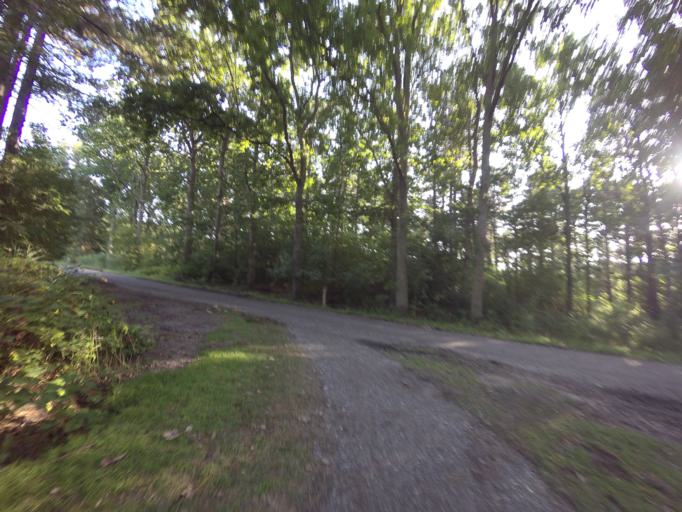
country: NL
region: Friesland
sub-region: Gemeente Terschelling
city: West-Terschelling
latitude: 53.3665
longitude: 5.2069
